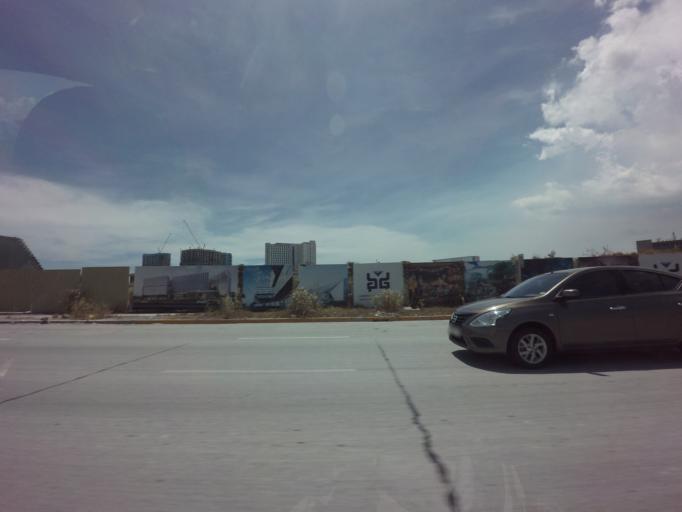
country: PH
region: Metro Manila
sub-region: Makati City
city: Makati City
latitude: 14.5170
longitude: 120.9849
